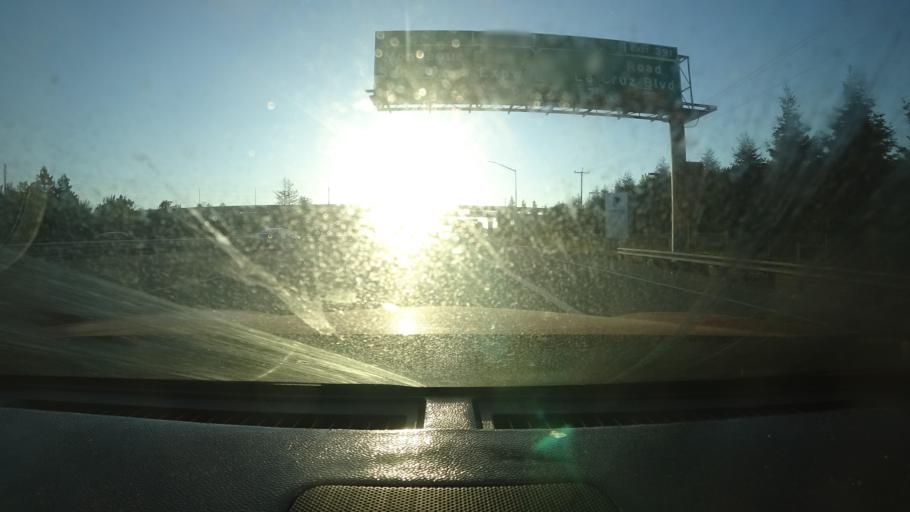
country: US
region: California
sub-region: Santa Clara County
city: Santa Clara
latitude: 37.3734
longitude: -121.9255
